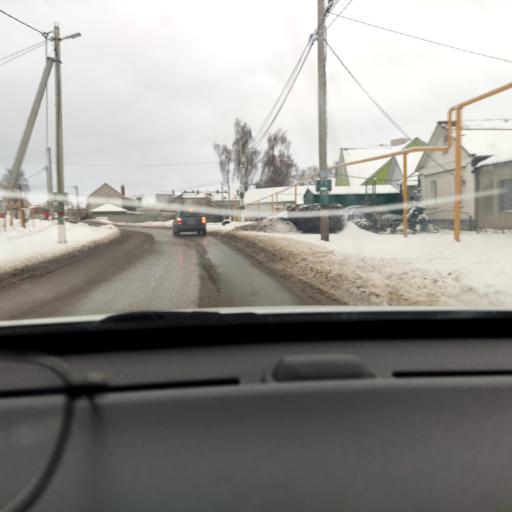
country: RU
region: Voronezj
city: Novaya Usman'
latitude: 51.6468
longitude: 39.4099
